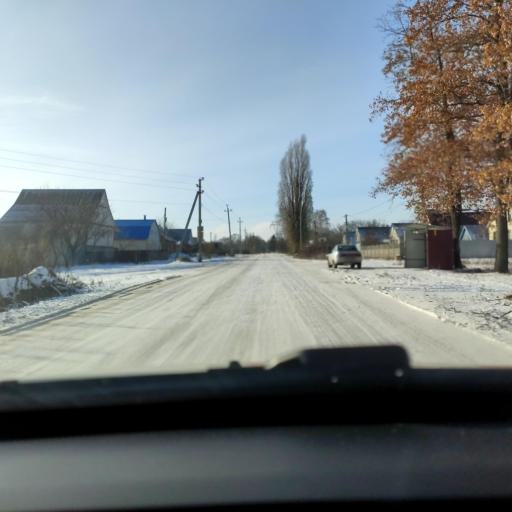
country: RU
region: Voronezj
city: Devitsa
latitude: 51.6035
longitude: 38.9825
